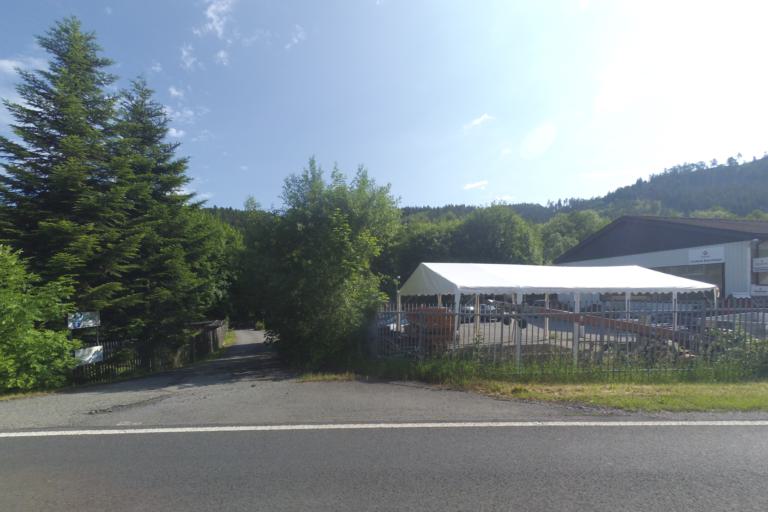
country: DE
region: Thuringia
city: Probstzella
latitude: 50.5248
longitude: 11.3900
